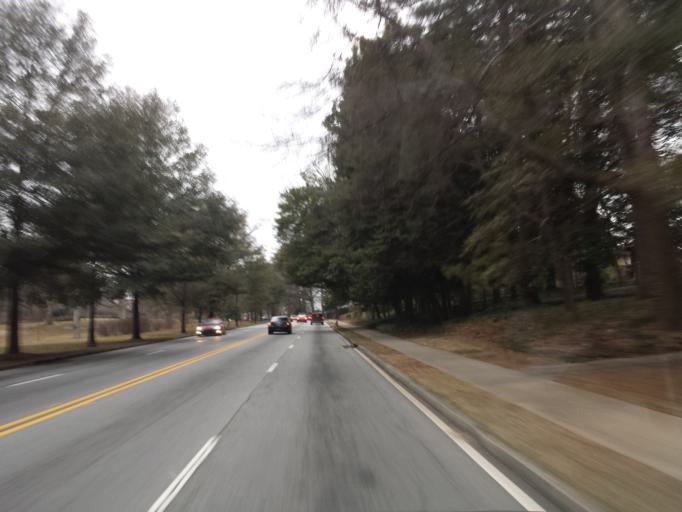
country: US
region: Georgia
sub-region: DeKalb County
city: Druid Hills
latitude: 33.7726
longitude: -84.3280
